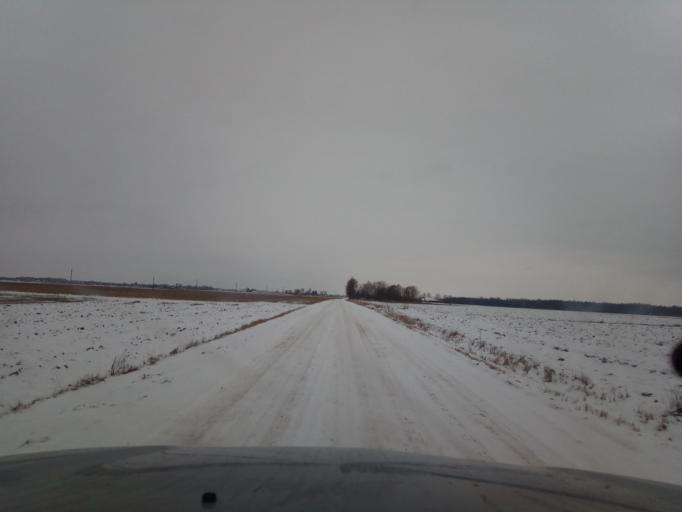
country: LT
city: Ramygala
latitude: 55.4939
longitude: 24.5425
